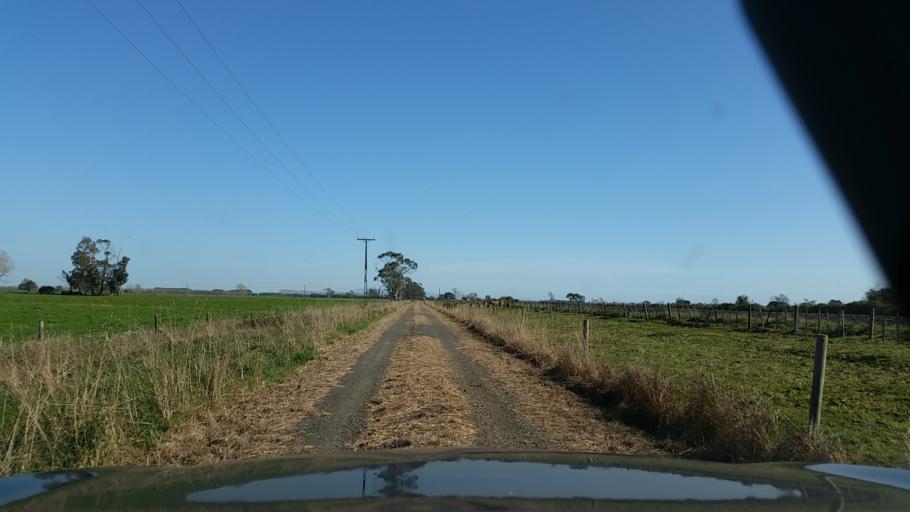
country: NZ
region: Waikato
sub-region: Waipa District
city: Cambridge
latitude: -37.6828
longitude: 175.4549
